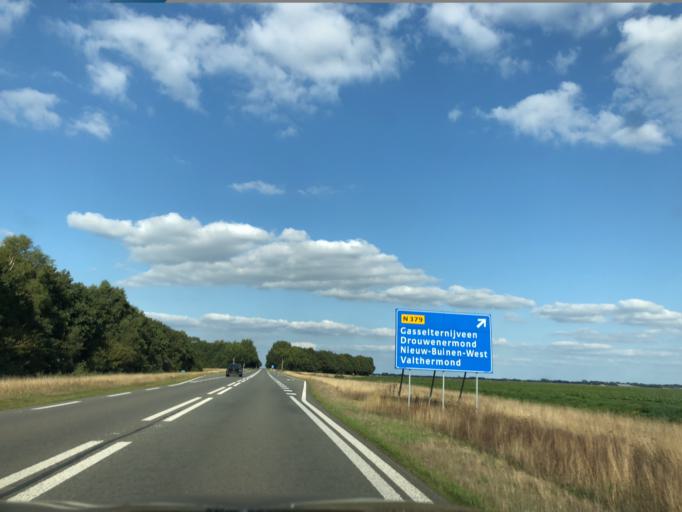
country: NL
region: Groningen
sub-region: Gemeente Stadskanaal
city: Stadskanaal
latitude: 52.9592
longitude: 6.8895
